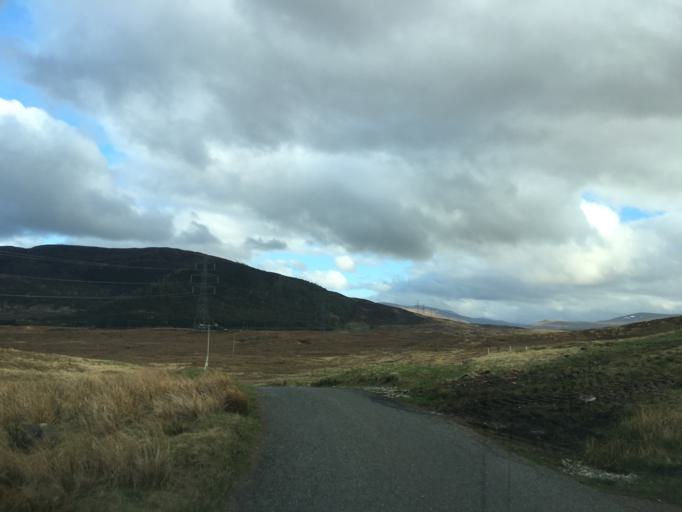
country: GB
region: Scotland
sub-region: Highland
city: Kingussie
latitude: 57.0101
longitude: -4.4149
